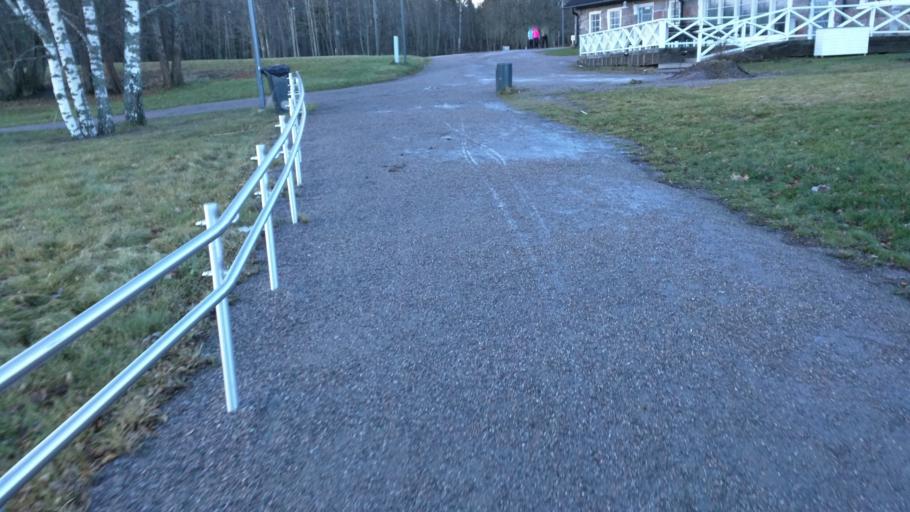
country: FI
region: Uusimaa
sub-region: Helsinki
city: Espoo
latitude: 60.2415
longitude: 24.6585
